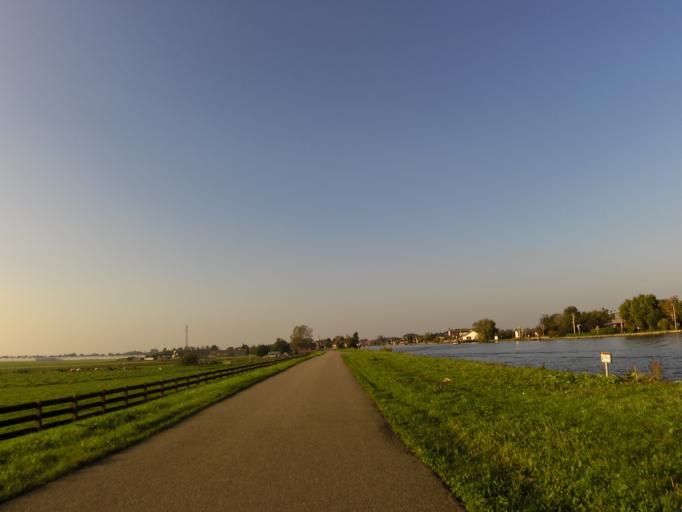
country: NL
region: South Holland
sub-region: Gemeente Alphen aan den Rijn
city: Alphen aan den Rijn
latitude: 52.1570
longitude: 4.6424
